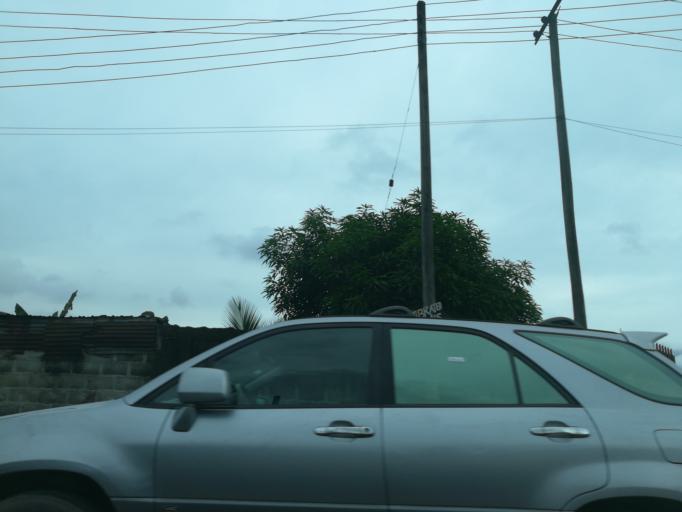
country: NG
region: Rivers
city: Port Harcourt
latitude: 4.8101
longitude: 6.9946
